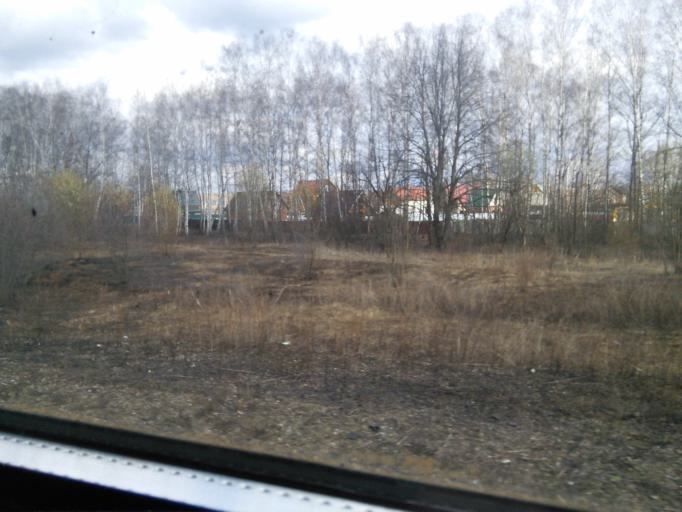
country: RU
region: Moskovskaya
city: L'vovskiy
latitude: 55.2883
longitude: 37.5075
